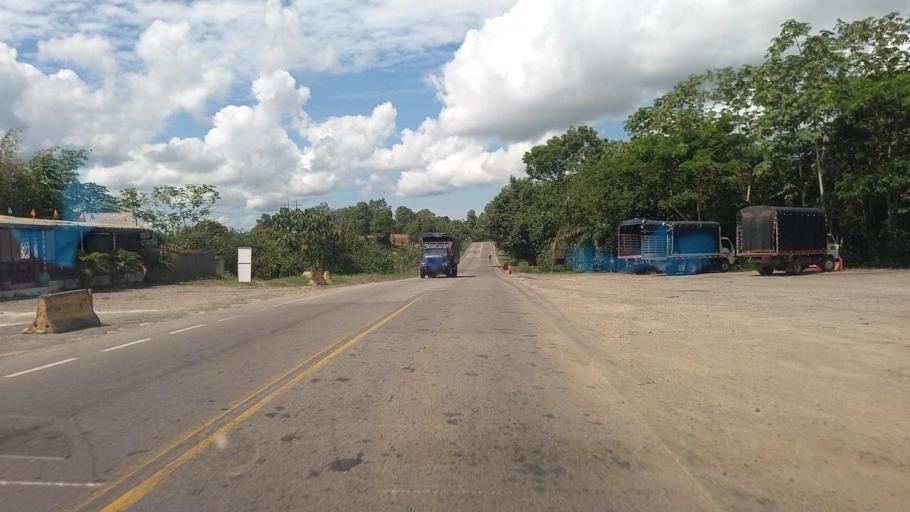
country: CO
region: Santander
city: Barrancabermeja
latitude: 7.1210
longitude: -73.5960
